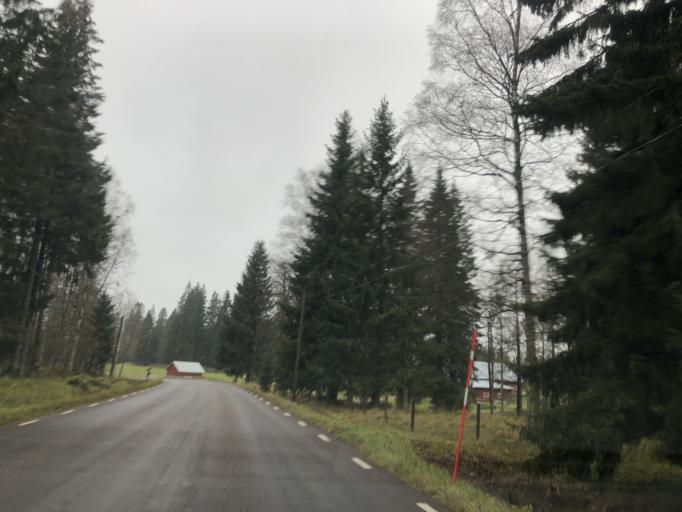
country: SE
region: Vaestra Goetaland
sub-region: Ulricehamns Kommun
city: Ulricehamn
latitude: 57.7620
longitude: 13.4793
